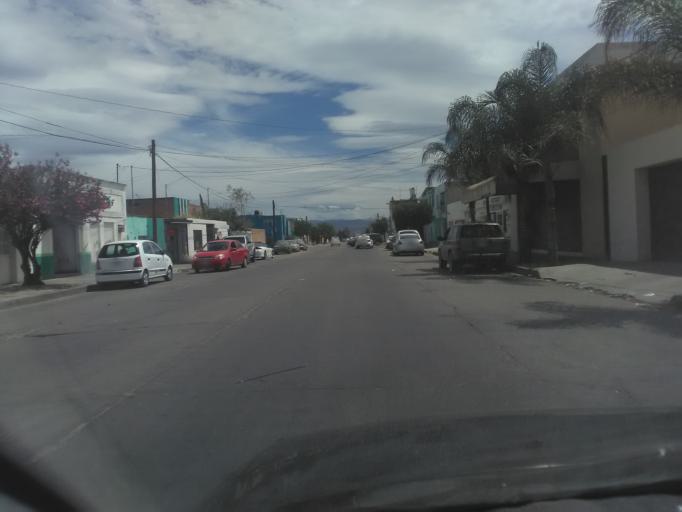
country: MX
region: Durango
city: Victoria de Durango
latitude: 24.0247
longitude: -104.6313
